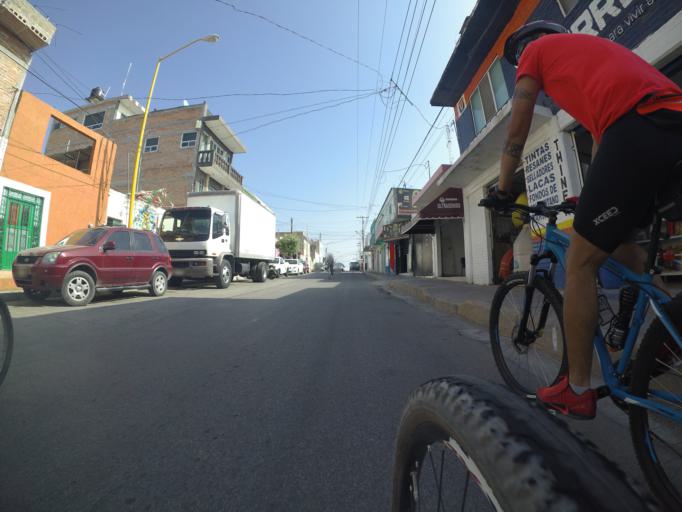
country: MX
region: Aguascalientes
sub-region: Jesus Maria
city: Jesus Maria
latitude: 21.9639
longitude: -102.3428
